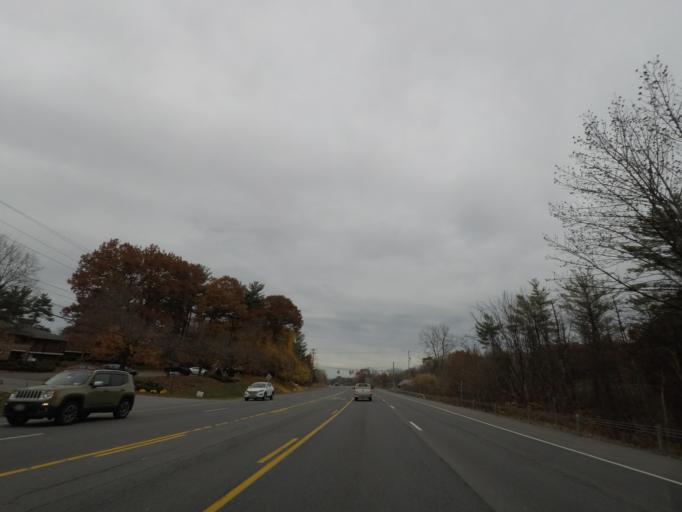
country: US
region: New York
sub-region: Saratoga County
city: Country Knolls
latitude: 42.8865
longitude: -73.7731
